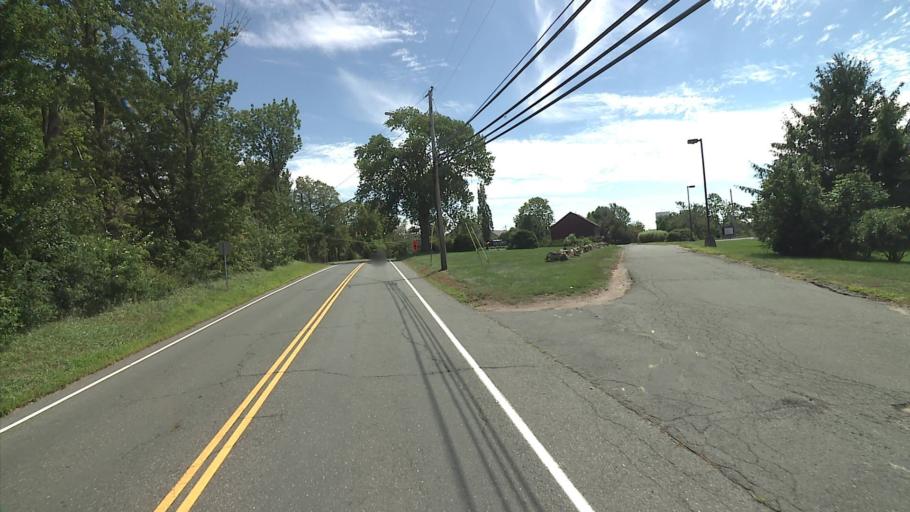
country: US
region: Connecticut
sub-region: Tolland County
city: Storrs
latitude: 41.8193
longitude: -72.2562
